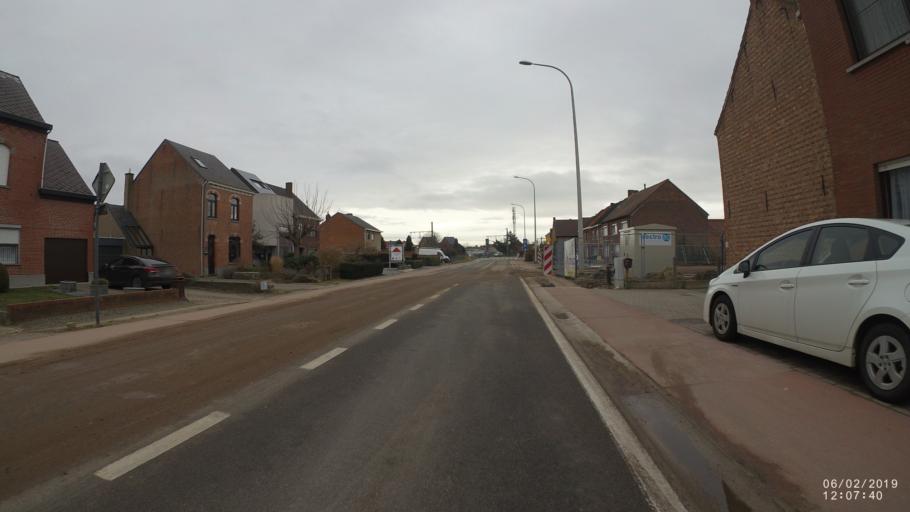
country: BE
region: Flanders
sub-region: Provincie Vlaams-Brabant
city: Aarschot
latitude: 50.9992
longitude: 4.8314
